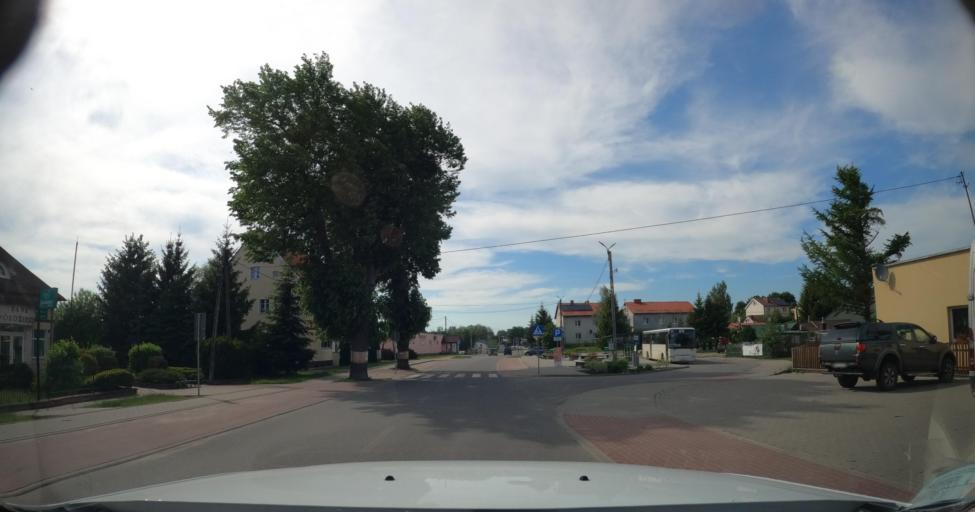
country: PL
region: Warmian-Masurian Voivodeship
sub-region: Powiat ostrodzki
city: Milakowo
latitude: 54.0101
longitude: 20.0673
